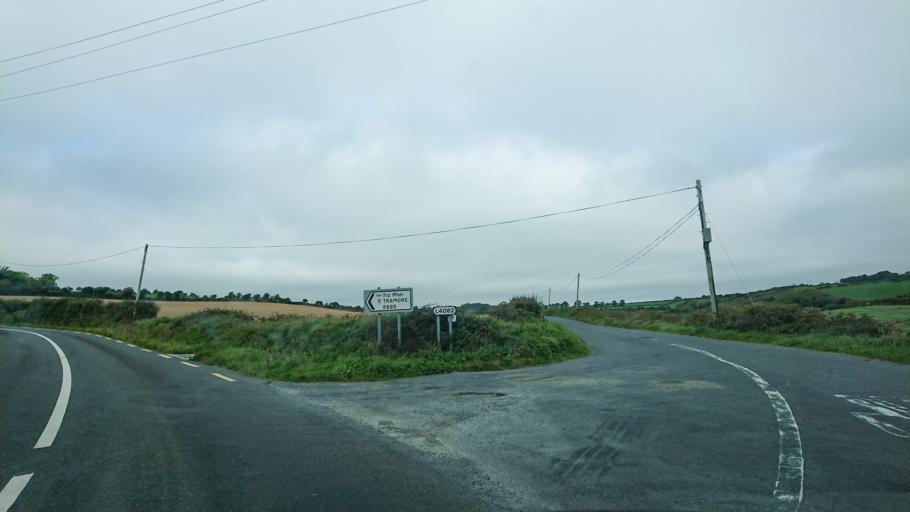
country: IE
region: Munster
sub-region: Waterford
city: Tra Mhor
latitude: 52.1823
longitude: -7.1146
